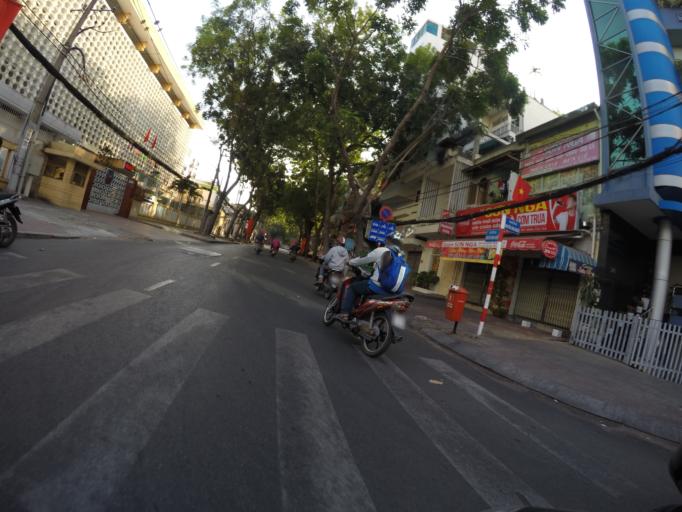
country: VN
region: Ho Chi Minh City
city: Quan Mot
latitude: 10.7905
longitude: 106.7015
